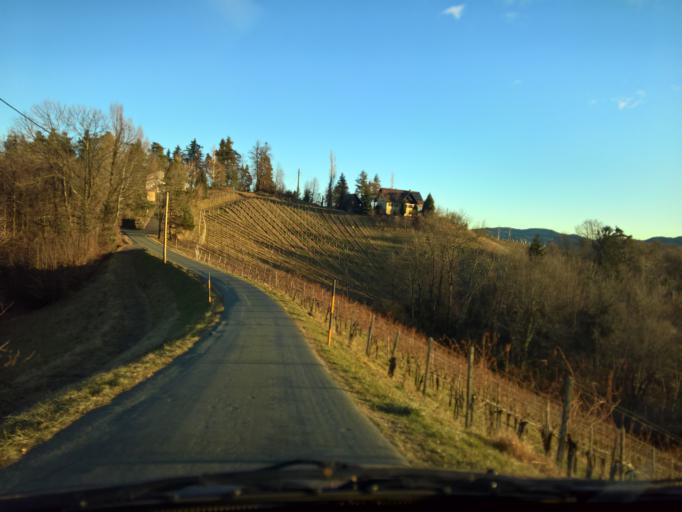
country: AT
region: Styria
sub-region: Politischer Bezirk Leibnitz
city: Leutschach
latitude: 46.6842
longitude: 15.4738
